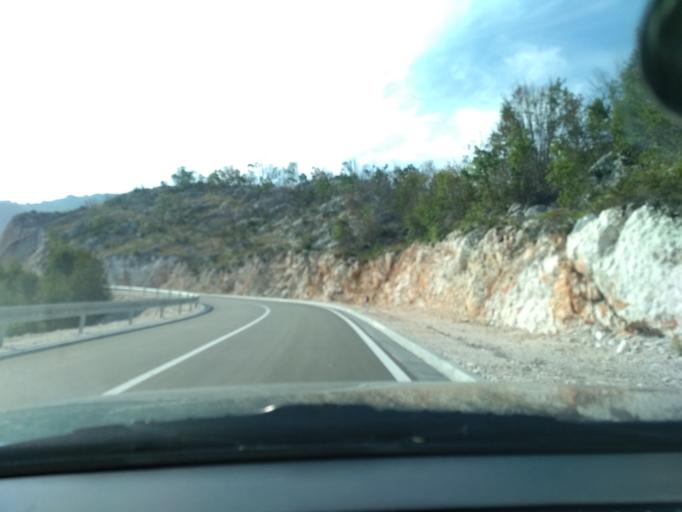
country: ME
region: Cetinje
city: Cetinje
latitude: 42.4254
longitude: 18.8729
